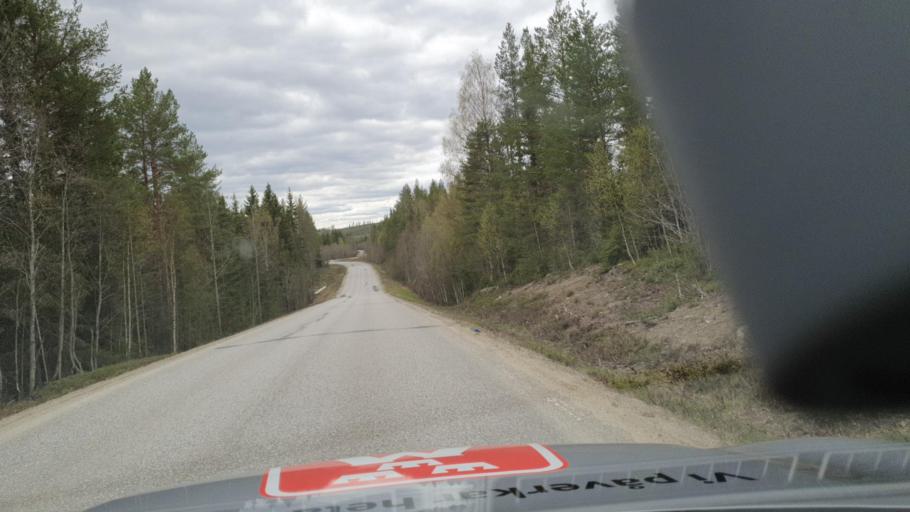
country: SE
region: Vaesternorrland
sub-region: OErnskoeldsviks Kommun
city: Ornskoldsvik
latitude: 63.6825
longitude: 18.7877
